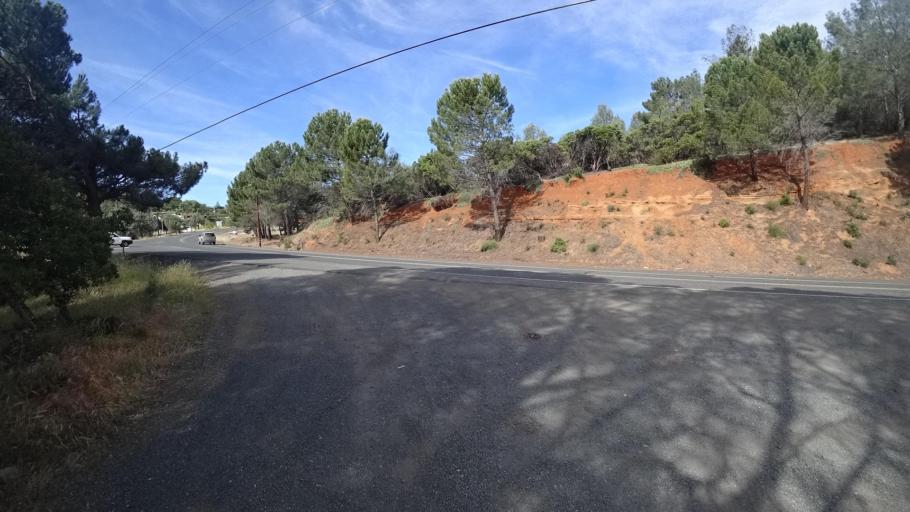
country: US
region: California
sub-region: Lake County
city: Soda Bay
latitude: 38.9549
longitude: -122.7271
